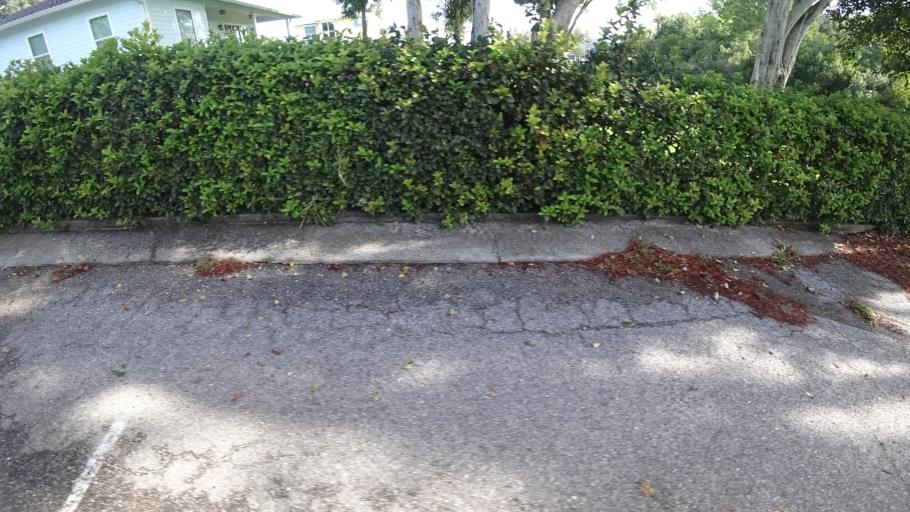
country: US
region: Florida
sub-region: Manatee County
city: West Bradenton
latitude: 27.5047
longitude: -82.6191
